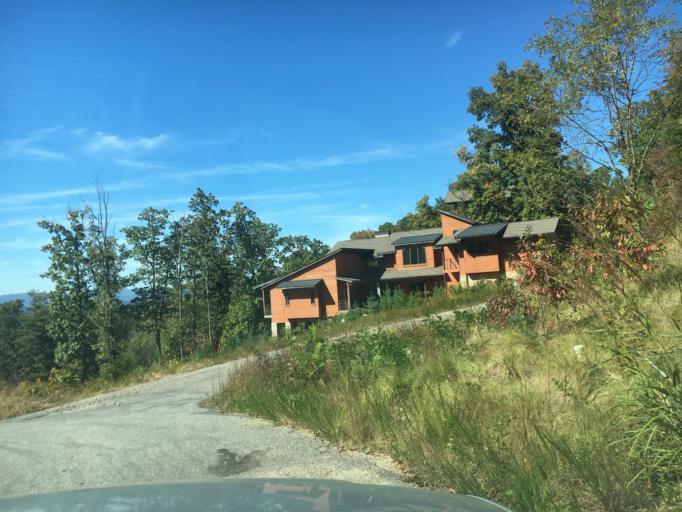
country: US
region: North Carolina
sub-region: Buncombe County
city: Woodfin
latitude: 35.6500
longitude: -82.5893
